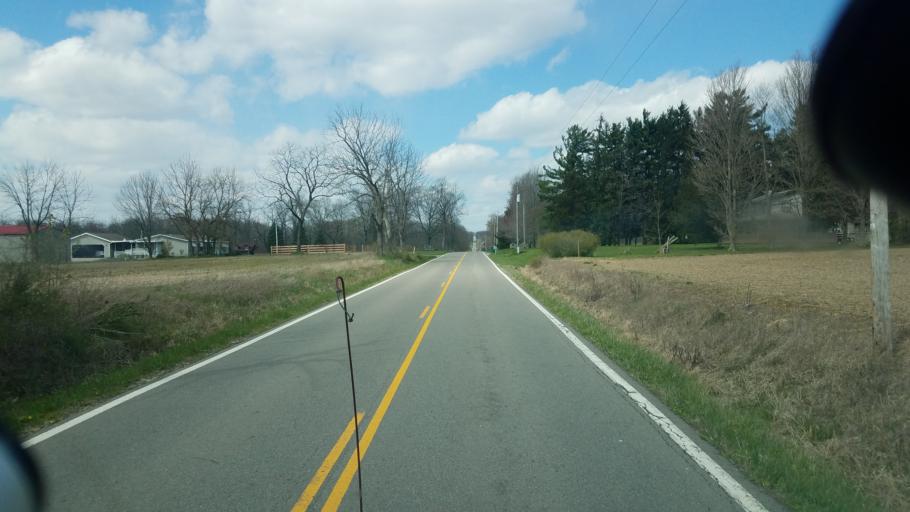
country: US
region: Ohio
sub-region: Licking County
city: Johnstown
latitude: 40.1275
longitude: -82.6149
